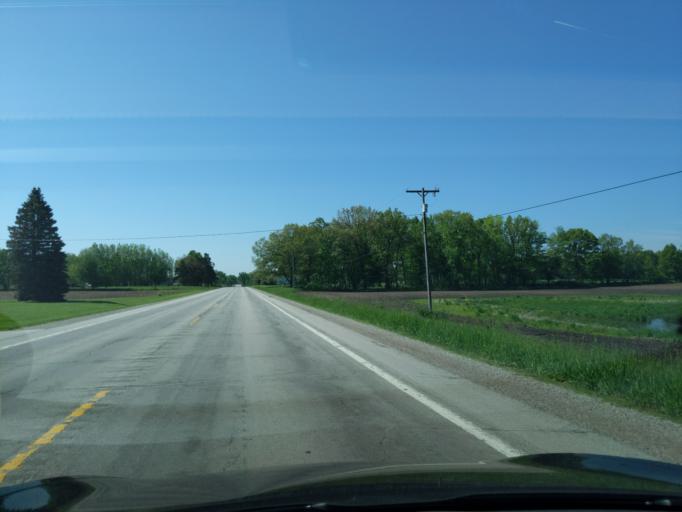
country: US
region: Michigan
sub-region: Ingham County
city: Stockbridge
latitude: 42.4993
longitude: -84.1902
